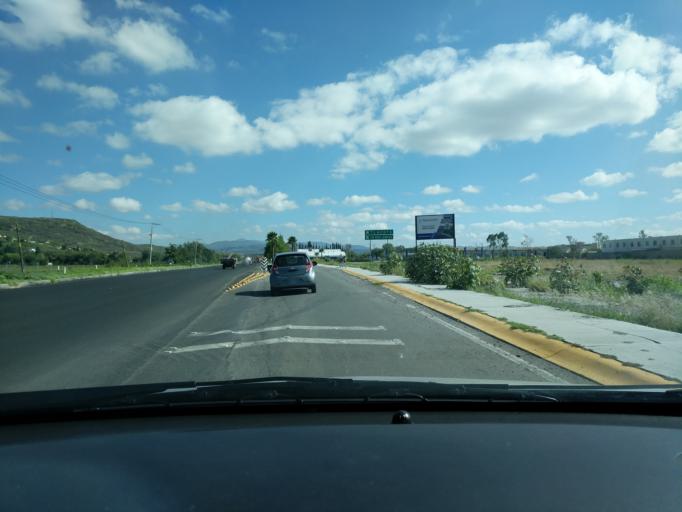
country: MX
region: Queretaro
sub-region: Queretaro
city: Patria Nueva
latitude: 20.6266
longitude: -100.4975
